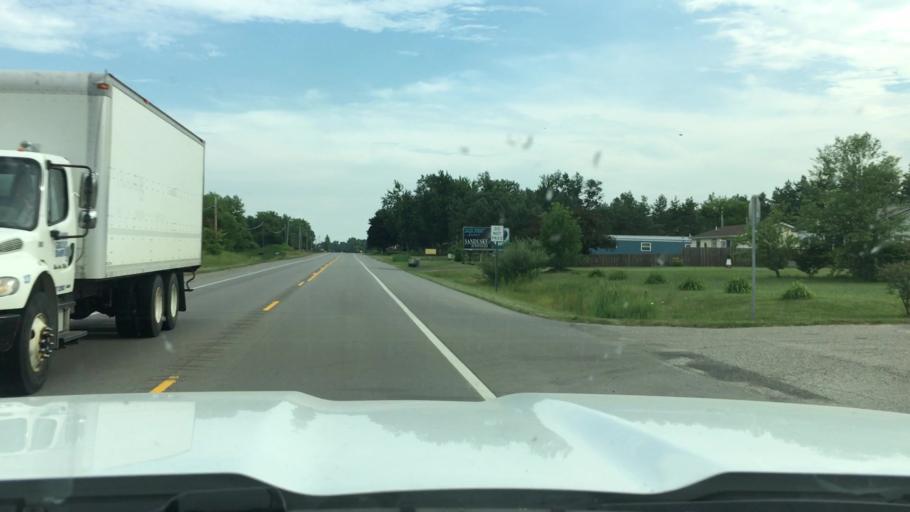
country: US
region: Michigan
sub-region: Sanilac County
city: Marlette
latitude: 43.3492
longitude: -83.0848
